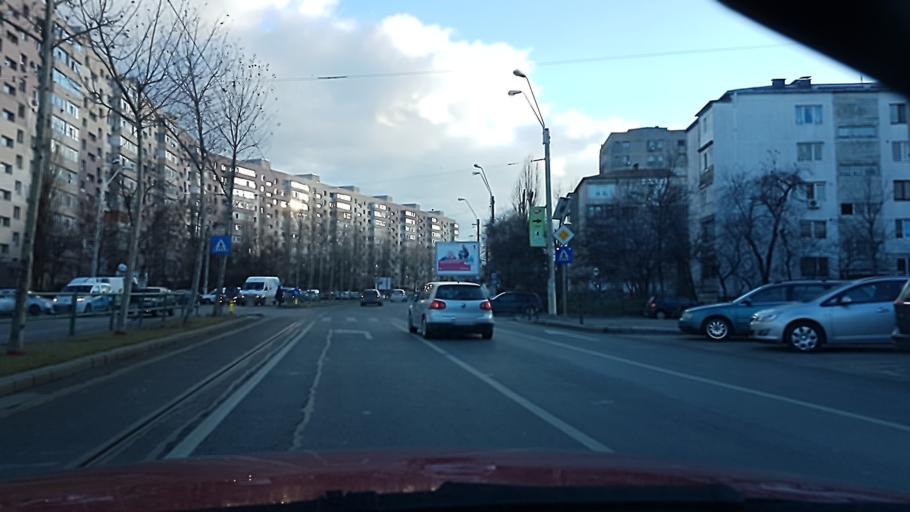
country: RO
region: Ilfov
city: Dobroesti
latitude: 44.4196
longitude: 26.1756
